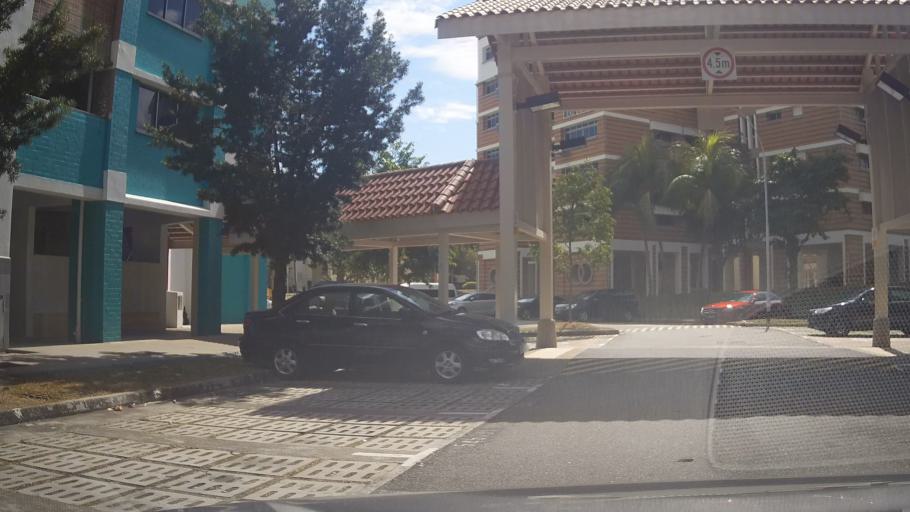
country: SG
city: Singapore
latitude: 1.3665
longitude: 103.9554
